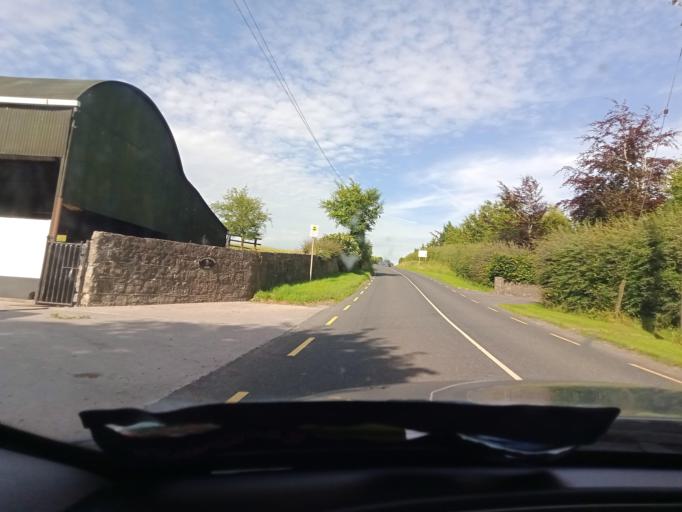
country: IE
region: Leinster
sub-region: An Iarmhi
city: Castlepollard
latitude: 53.6161
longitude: -7.2821
